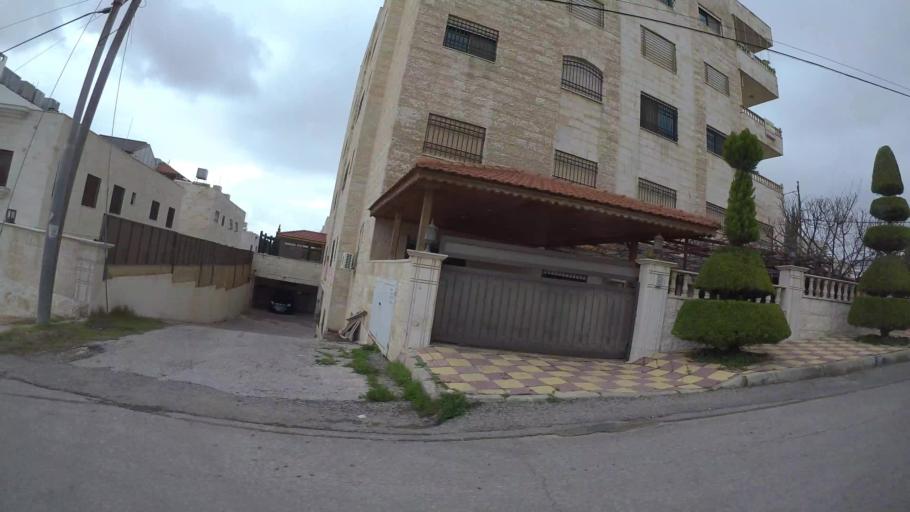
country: JO
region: Amman
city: Wadi as Sir
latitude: 31.9633
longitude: 35.8299
